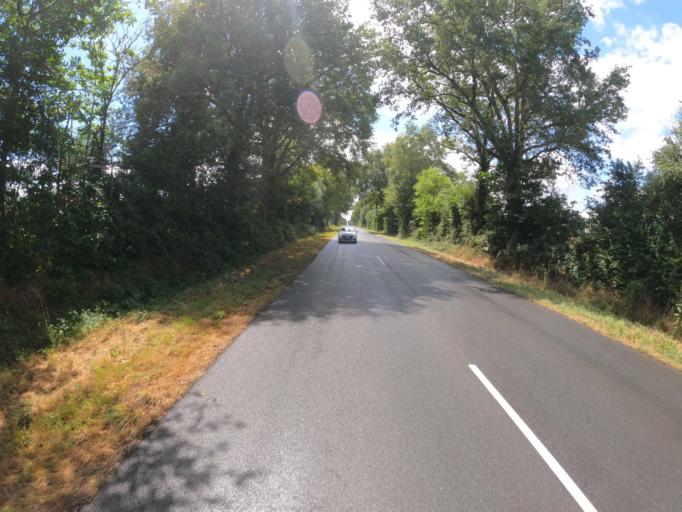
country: FR
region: Pays de la Loire
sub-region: Departement de Maine-et-Loire
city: Feneu
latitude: 47.5938
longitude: -0.5890
